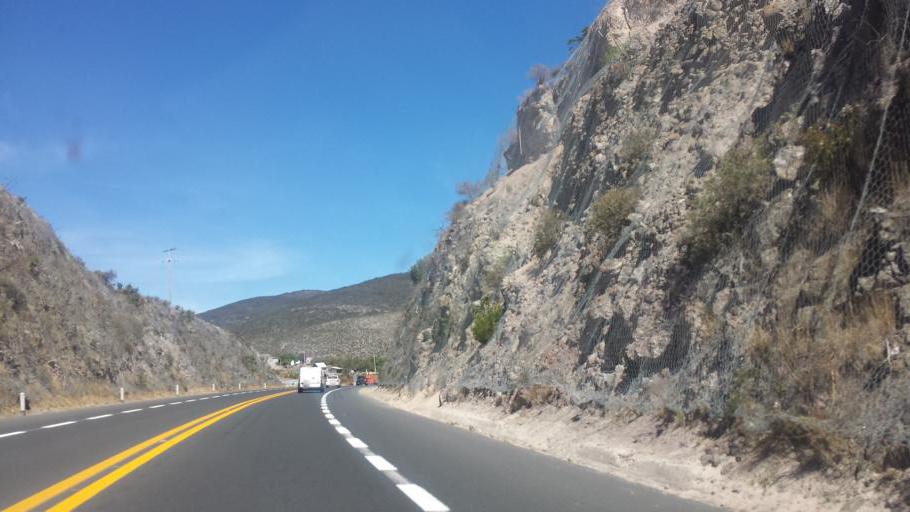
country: MX
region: Oaxaca
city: San Gabriel Casa Blanca
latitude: 17.9771
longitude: -97.3574
